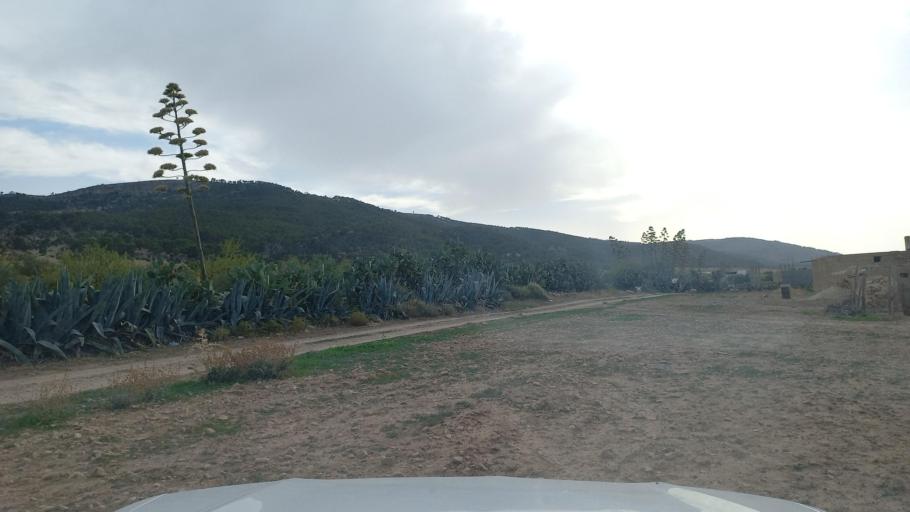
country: TN
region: Al Qasrayn
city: Kasserine
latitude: 35.3352
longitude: 8.8500
